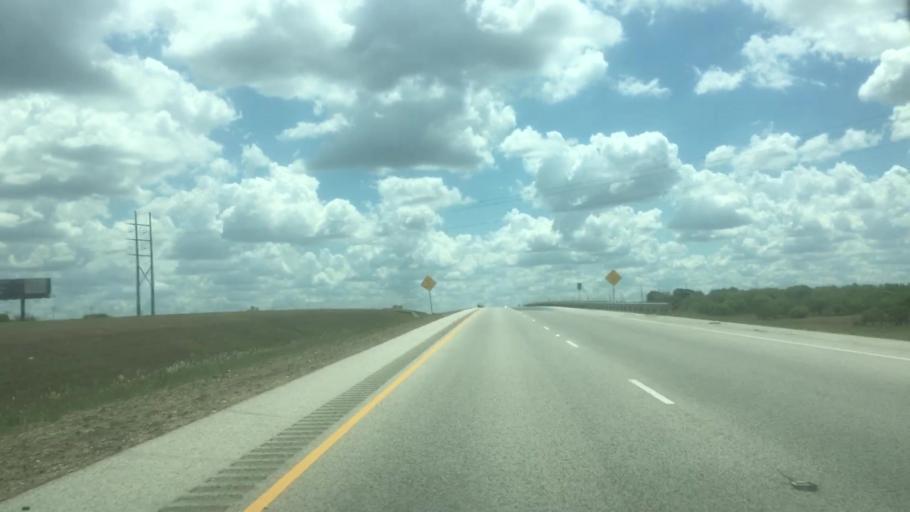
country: US
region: Texas
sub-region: Caldwell County
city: Uhland
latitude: 30.0085
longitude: -97.6878
